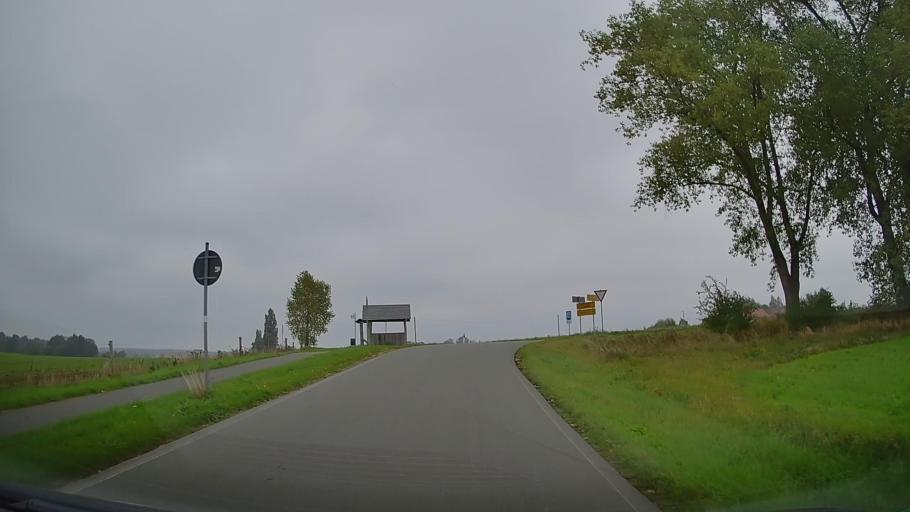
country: DE
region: Mecklenburg-Vorpommern
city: Neubukow
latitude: 54.0639
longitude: 11.6260
